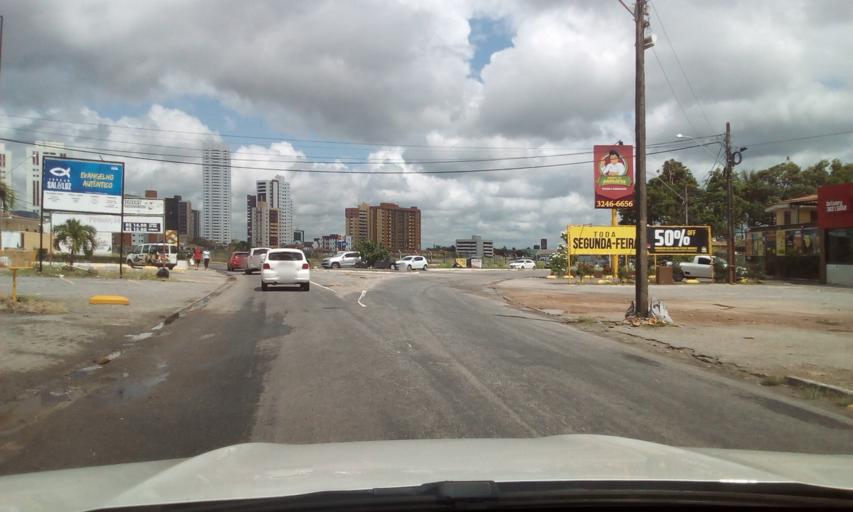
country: BR
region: Paraiba
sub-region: Joao Pessoa
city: Joao Pessoa
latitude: -7.0946
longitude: -34.8370
